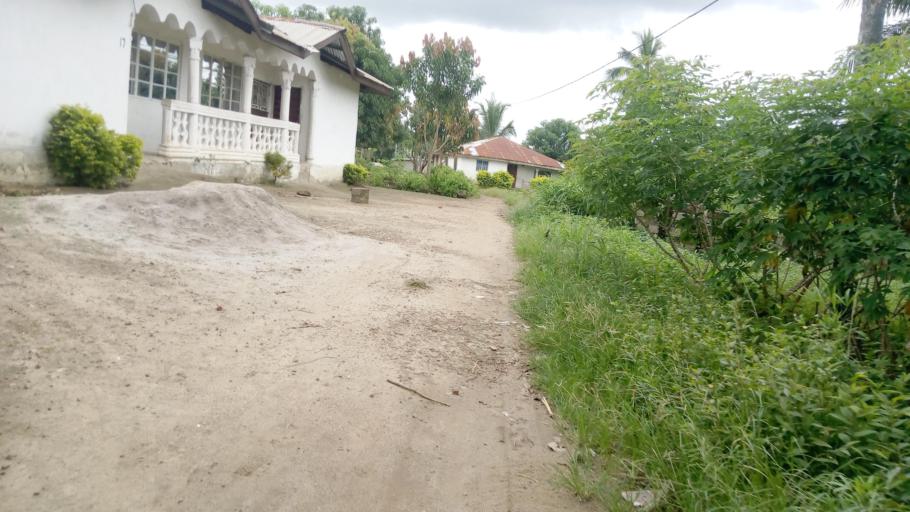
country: SL
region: Northern Province
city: Makeni
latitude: 8.8949
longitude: -12.0293
